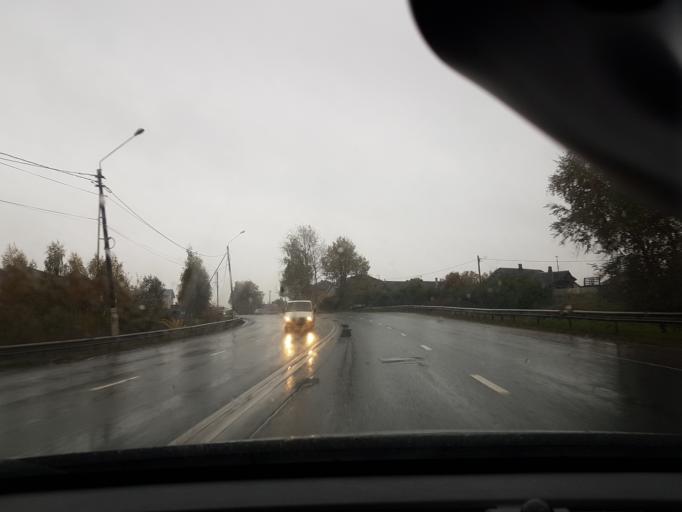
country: RU
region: Moskovskaya
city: Istra
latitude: 55.9093
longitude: 36.8762
